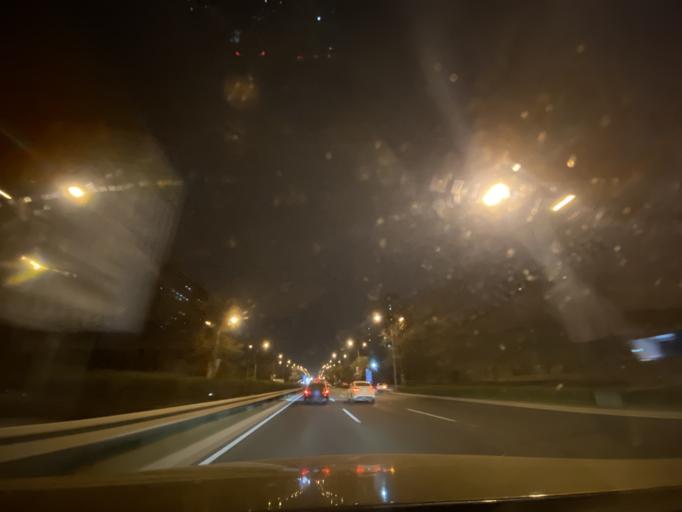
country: CN
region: Beijing
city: Lugouqiao
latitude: 39.8958
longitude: 116.2945
